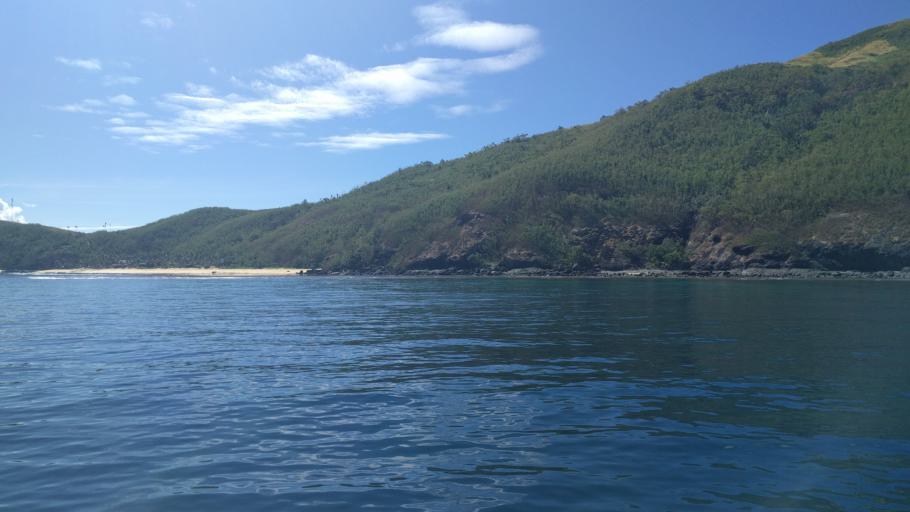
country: FJ
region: Western
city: Lautoka
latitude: -17.2818
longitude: 177.1032
